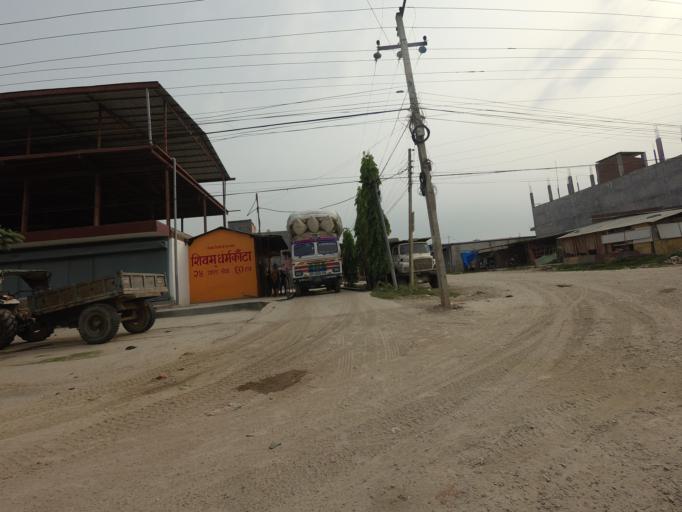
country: NP
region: Western Region
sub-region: Lumbini Zone
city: Bhairahawa
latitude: 27.5084
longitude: 83.4366
